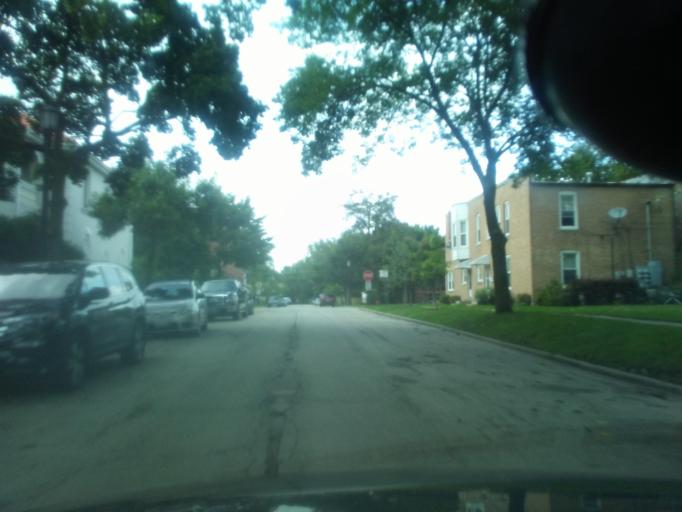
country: US
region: Illinois
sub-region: Cook County
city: Evanston
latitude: 42.0323
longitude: -87.6923
